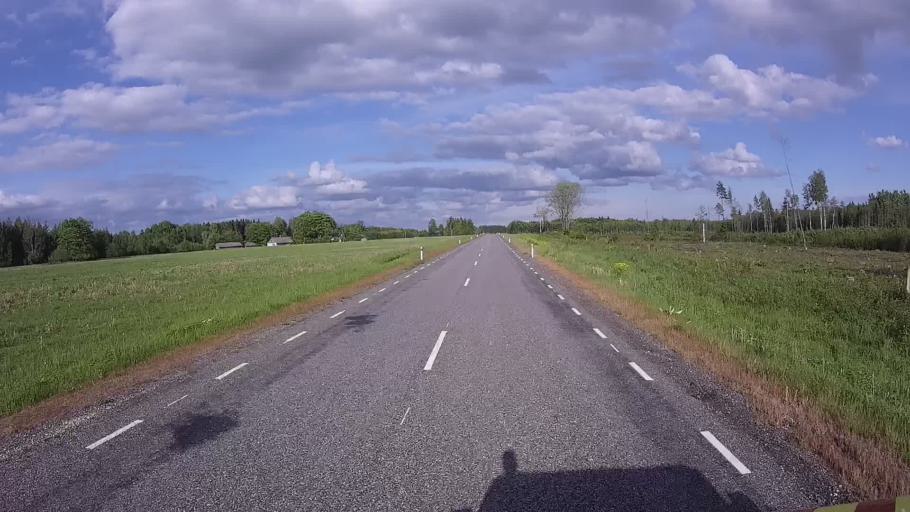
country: EE
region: Jogevamaa
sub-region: Mustvee linn
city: Mustvee
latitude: 59.0259
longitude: 26.9983
